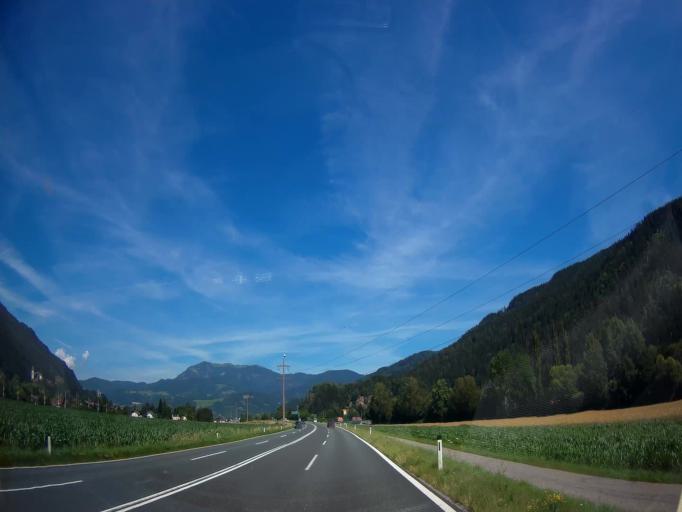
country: AT
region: Carinthia
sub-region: Politischer Bezirk Sankt Veit an der Glan
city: Friesach
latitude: 46.9469
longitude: 14.4220
